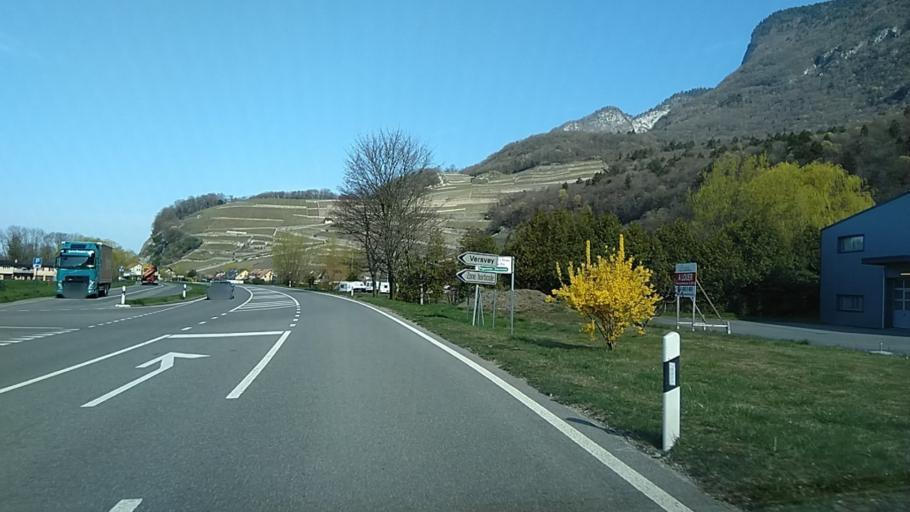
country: CH
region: Vaud
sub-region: Aigle District
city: Aigle
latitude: 46.3448
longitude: 6.9426
